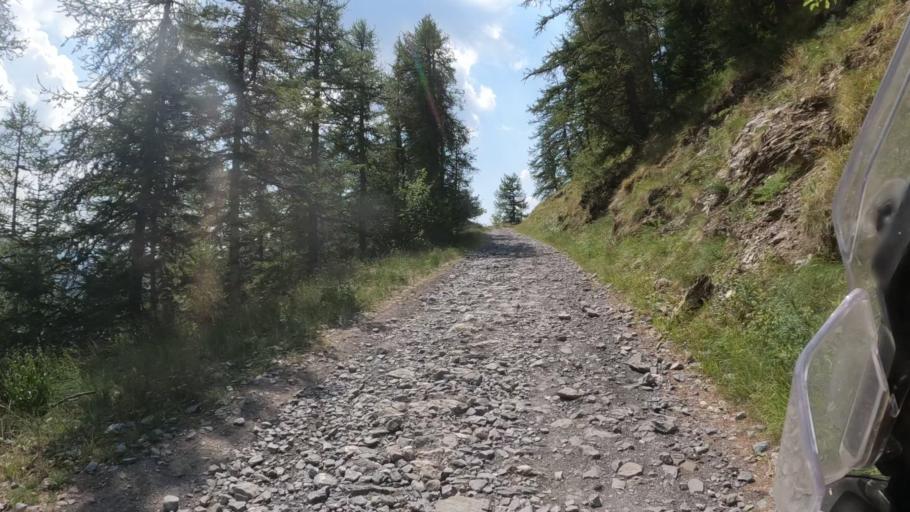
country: IT
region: Piedmont
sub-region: Provincia di Cuneo
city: Briga Alta
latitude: 44.0439
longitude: 7.7049
